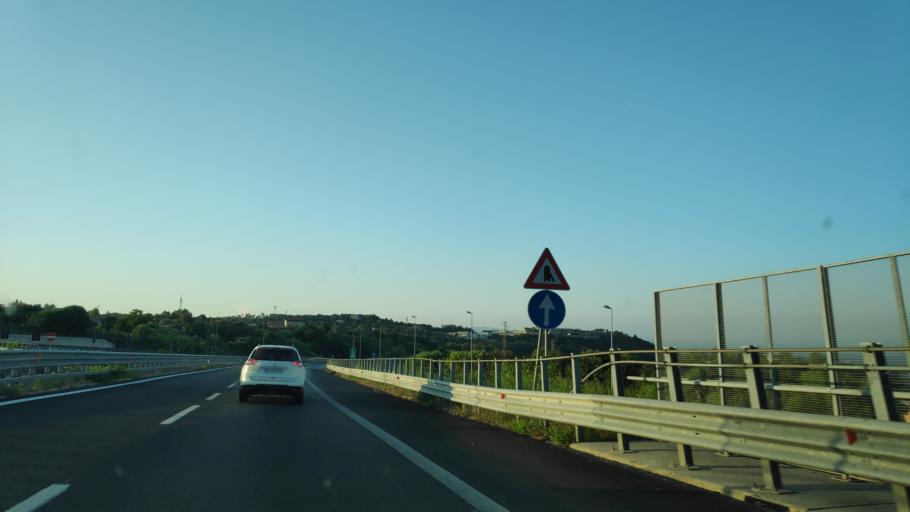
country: IT
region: Calabria
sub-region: Provincia di Reggio Calabria
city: Seminara
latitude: 38.3671
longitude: 15.8657
